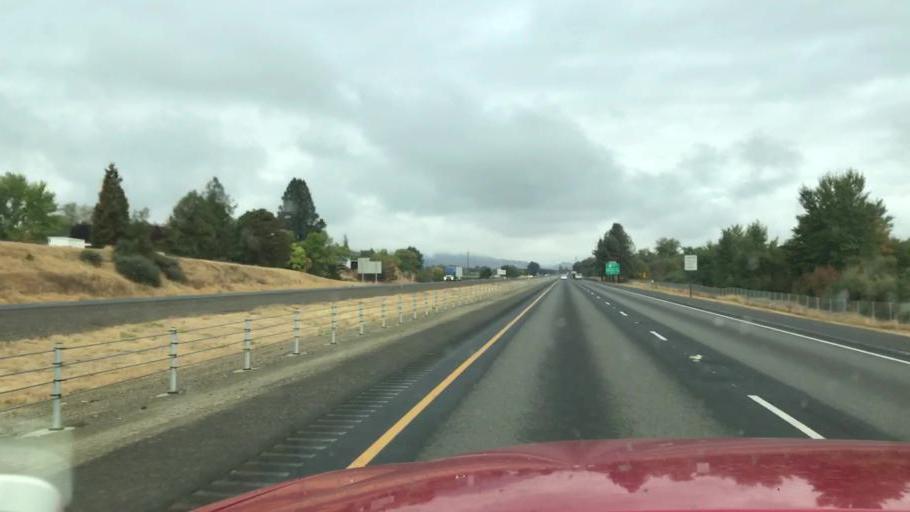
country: US
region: Oregon
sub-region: Jackson County
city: Central Point
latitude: 42.3919
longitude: -122.9219
